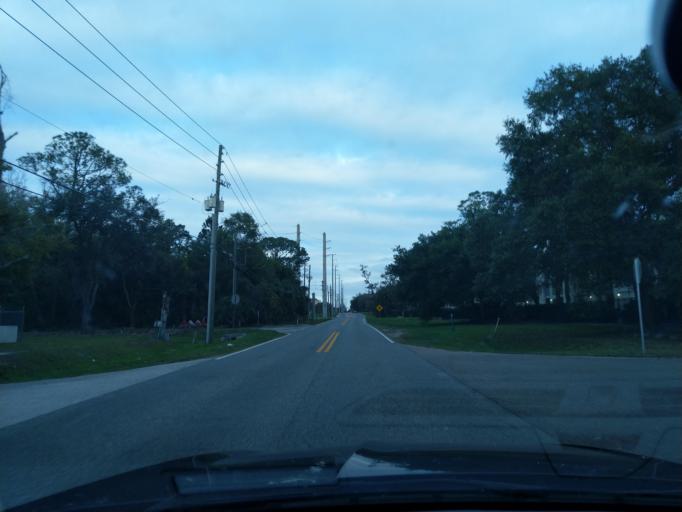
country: US
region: Florida
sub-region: Orange County
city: Doctor Phillips
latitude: 28.3914
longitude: -81.5046
